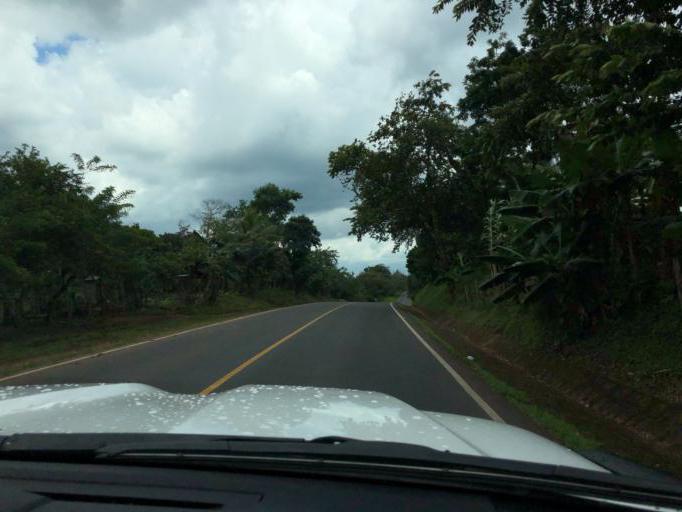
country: NI
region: Chontales
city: Villa Sandino
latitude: 11.9960
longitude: -84.8537
